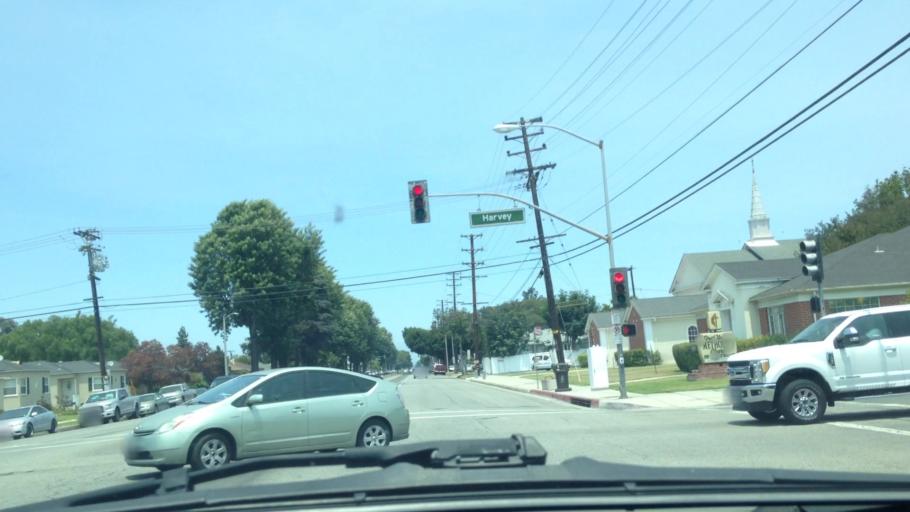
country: US
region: California
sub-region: Los Angeles County
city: Lakewood
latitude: 33.8360
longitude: -118.1251
